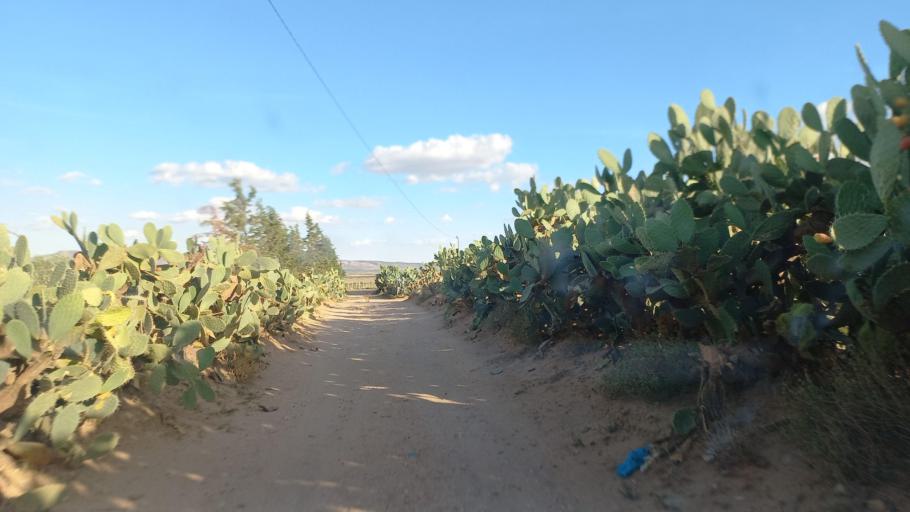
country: TN
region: Al Qasrayn
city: Sbiba
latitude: 35.3799
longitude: 9.0219
